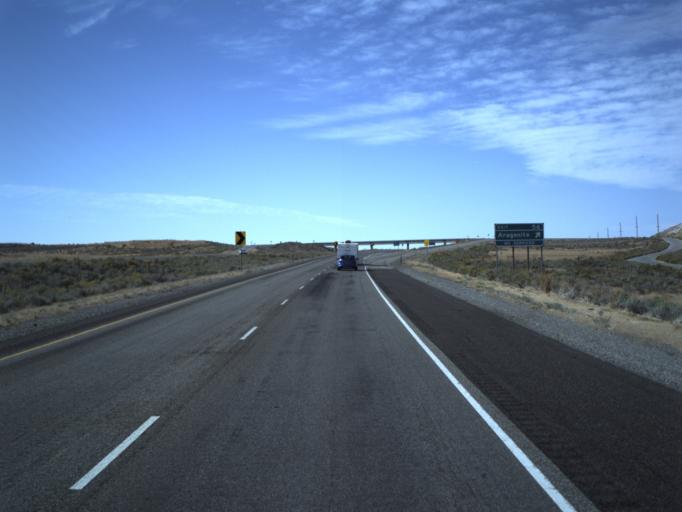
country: US
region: Utah
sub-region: Tooele County
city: Grantsville
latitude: 40.7730
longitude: -112.9780
